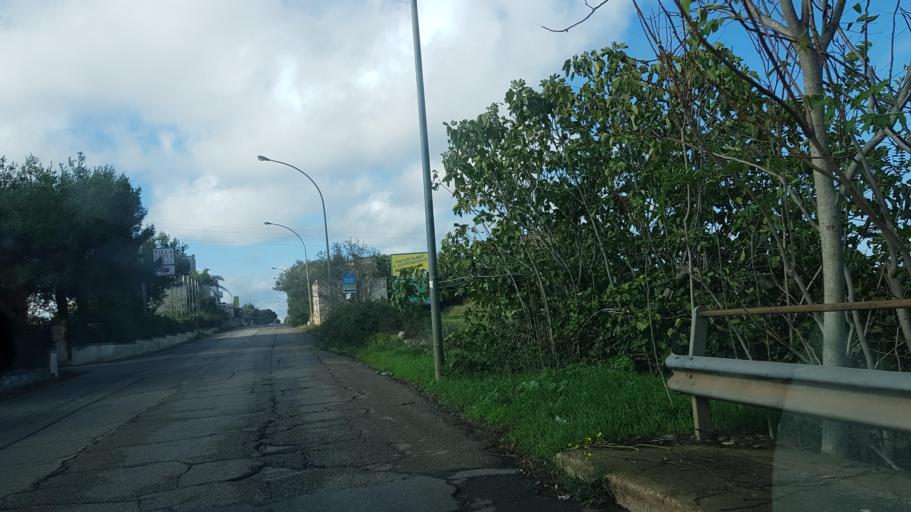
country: IT
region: Apulia
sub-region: Provincia di Brindisi
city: Carovigno
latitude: 40.7060
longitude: 17.6504
